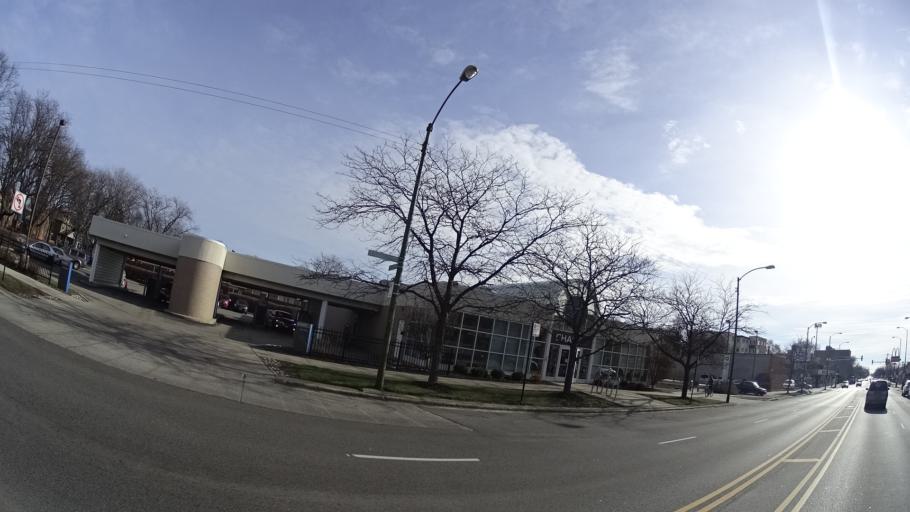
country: US
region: Illinois
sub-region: Cook County
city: Evanston
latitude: 42.0096
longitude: -87.6902
